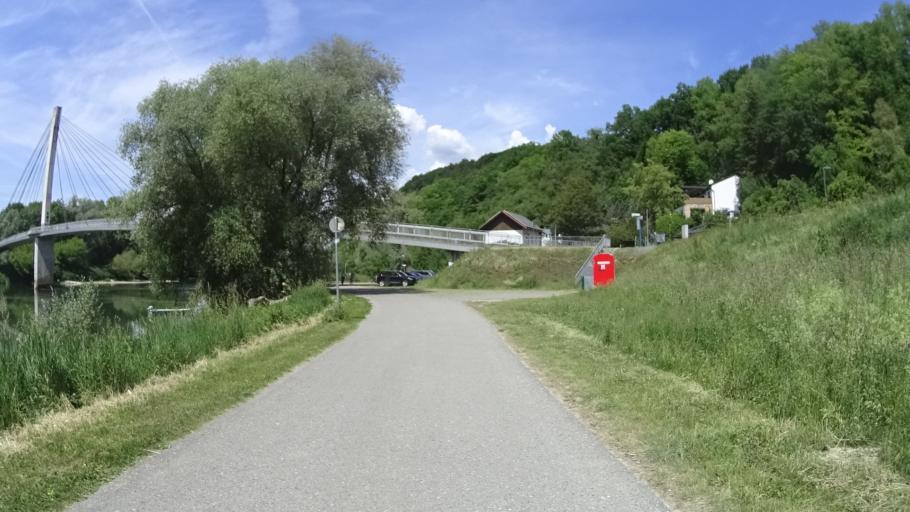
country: DE
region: Bavaria
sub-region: Lower Bavaria
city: Bad Abbach
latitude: 48.9401
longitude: 12.0392
